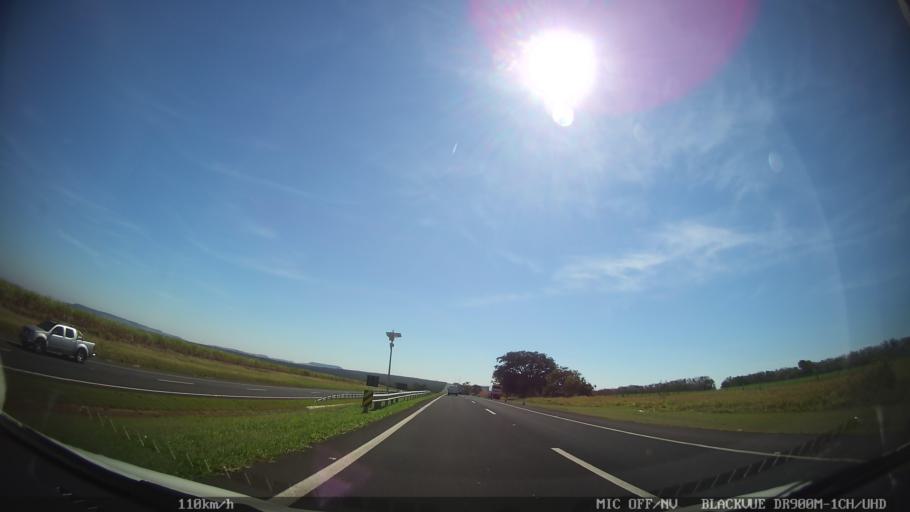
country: BR
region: Sao Paulo
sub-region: Santa Rita Do Passa Quatro
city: Santa Rita do Passa Quatro
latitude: -21.6489
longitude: -47.6105
